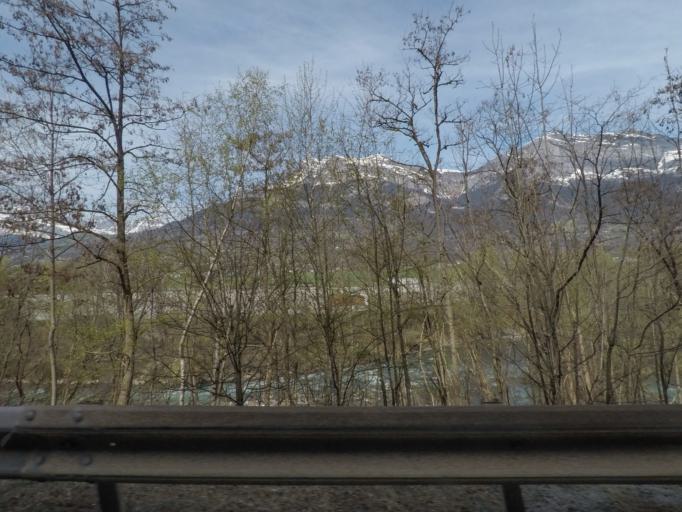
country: FR
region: Rhone-Alpes
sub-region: Departement de la Haute-Savoie
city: Saint-Gervais-les-Bains
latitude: 45.9136
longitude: 6.7226
